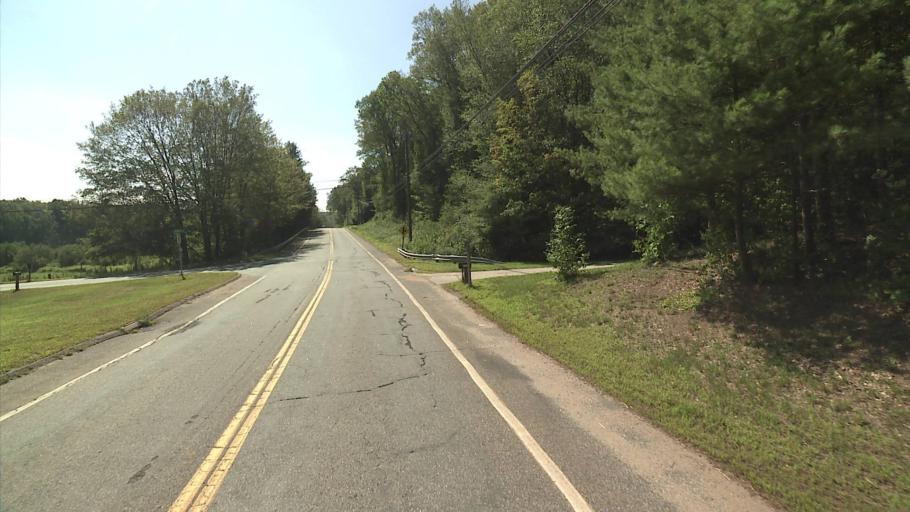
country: US
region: Connecticut
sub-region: Tolland County
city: Storrs
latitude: 41.8790
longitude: -72.1629
